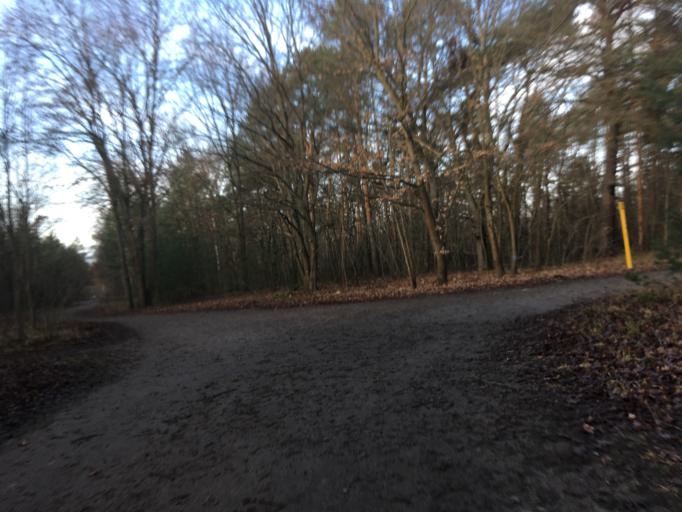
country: DE
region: Berlin
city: Johannisthal
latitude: 52.4522
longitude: 13.4932
